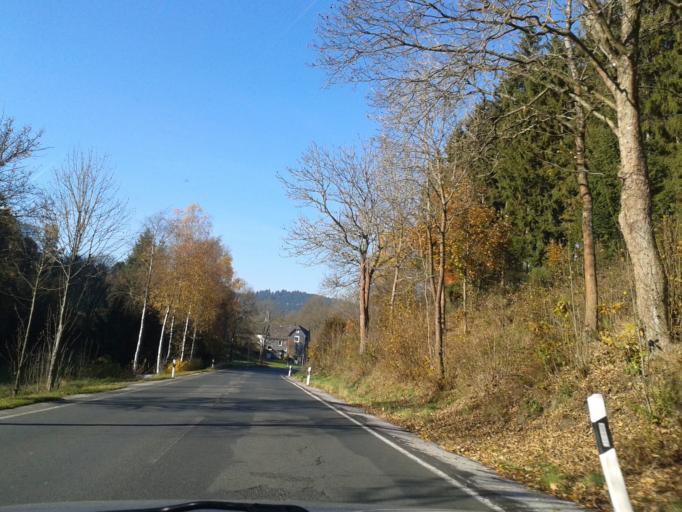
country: DE
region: North Rhine-Westphalia
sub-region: Regierungsbezirk Arnsberg
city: Bad Laasphe
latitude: 50.8705
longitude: 8.3588
